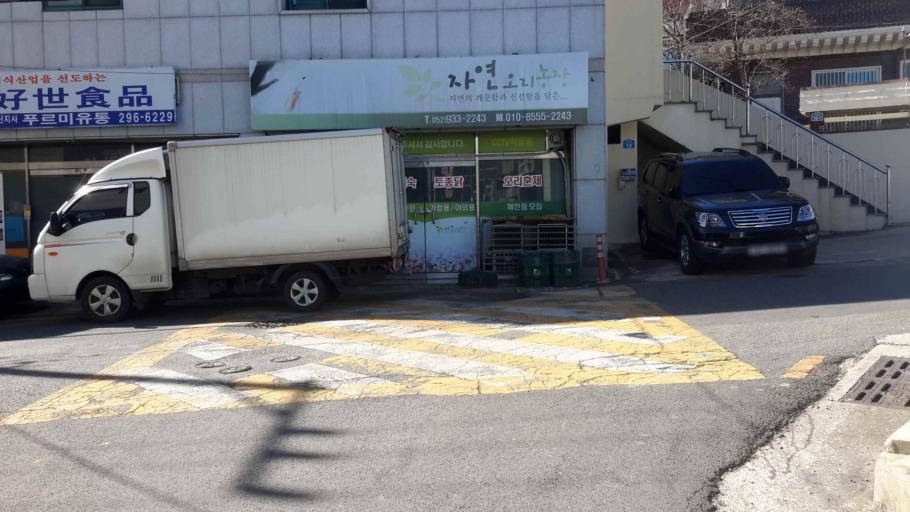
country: KR
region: Ulsan
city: Ulsan
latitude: 35.5615
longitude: 129.3402
